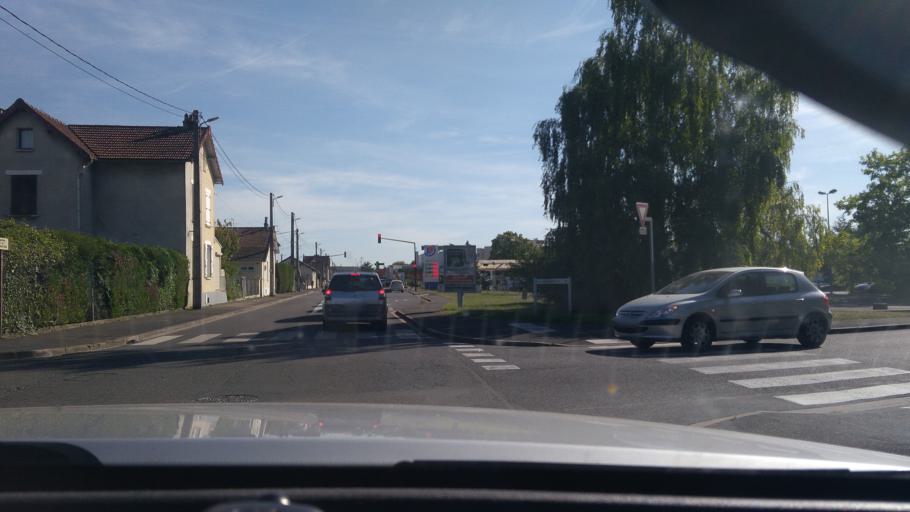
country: FR
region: Ile-de-France
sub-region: Departement de Seine-et-Marne
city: Montereau-Fault-Yonne
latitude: 48.3748
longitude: 2.9441
